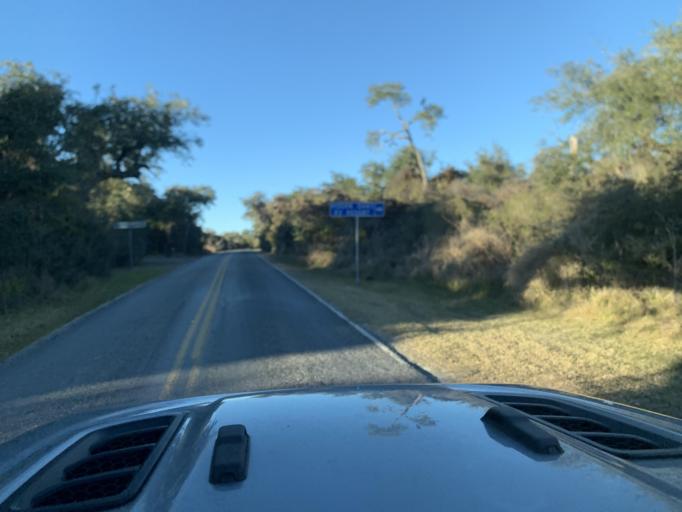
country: US
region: Texas
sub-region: Aransas County
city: Fulton
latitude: 28.1430
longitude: -96.9843
